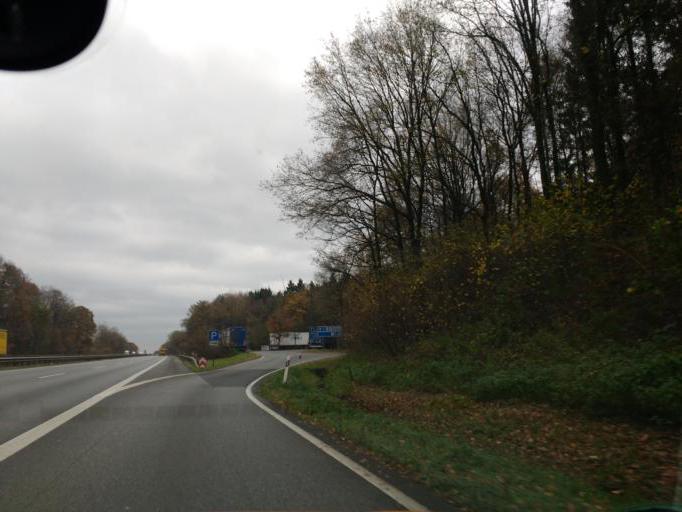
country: DE
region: Lower Saxony
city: Hauslingen
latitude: 52.8872
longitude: 9.4516
